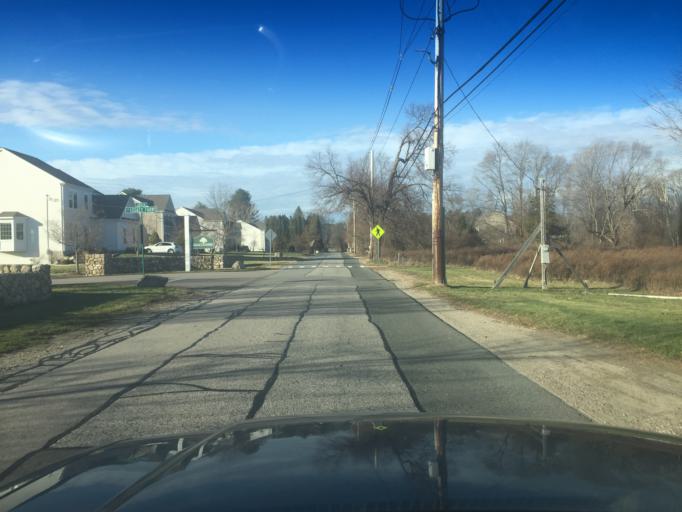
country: US
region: Massachusetts
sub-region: Middlesex County
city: Hopkinton
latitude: 42.2326
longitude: -71.4882
